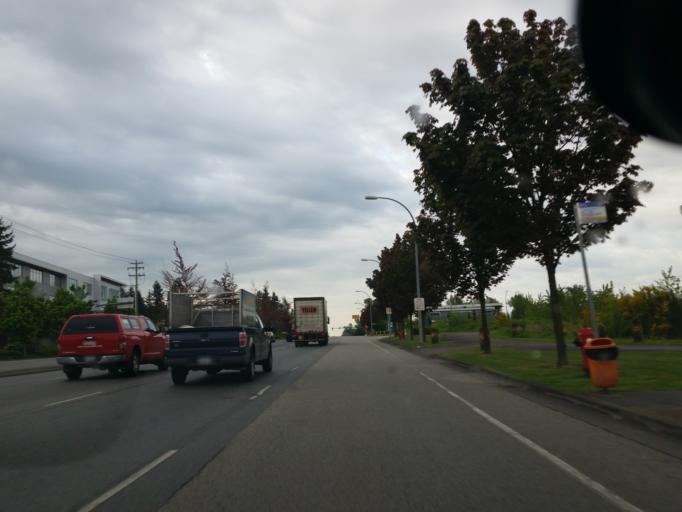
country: CA
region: British Columbia
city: Walnut Grove
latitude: 49.1587
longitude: -122.6682
